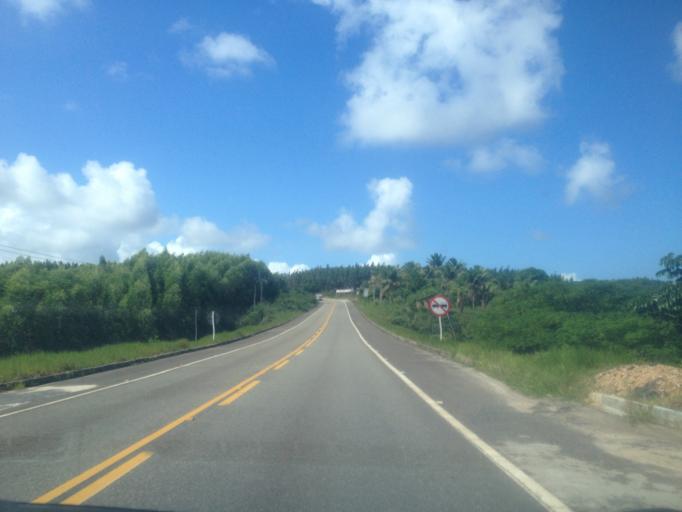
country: BR
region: Sergipe
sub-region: Indiaroba
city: Indiaroba
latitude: -11.4866
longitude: -37.4738
